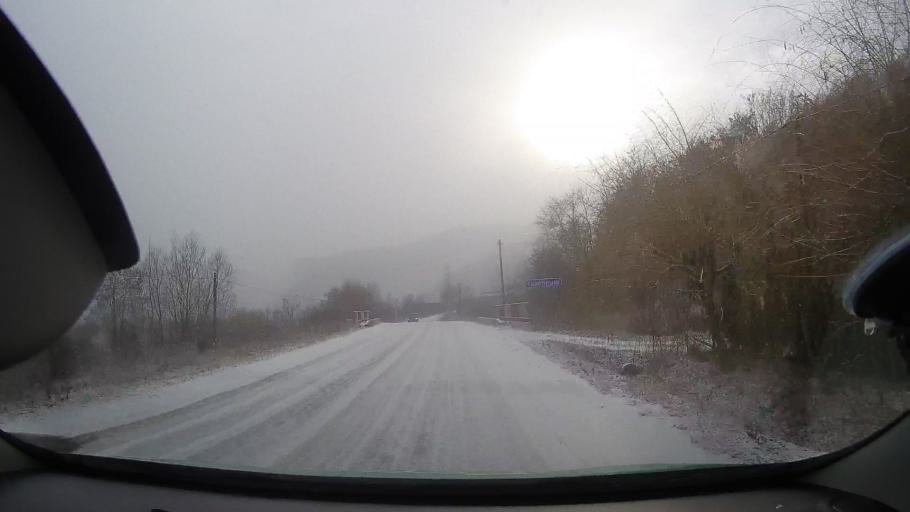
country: RO
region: Alba
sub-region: Comuna Rimetea
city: Rimetea
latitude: 46.3933
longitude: 23.5606
